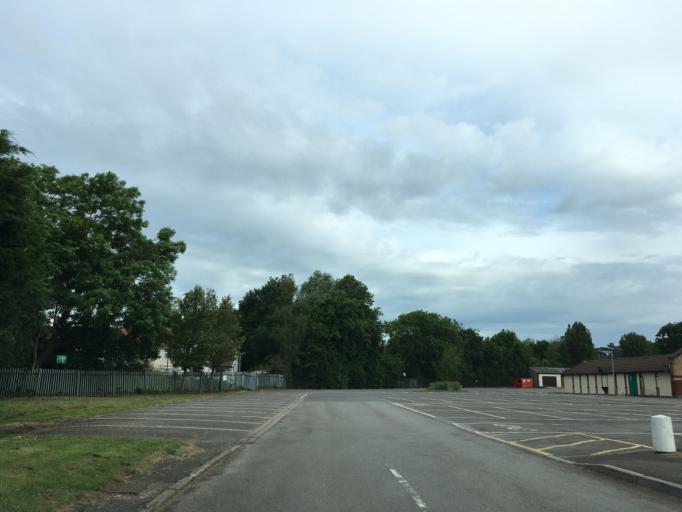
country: GB
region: England
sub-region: South Gloucestershire
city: Stoke Gifford
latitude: 51.5050
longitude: -2.5878
